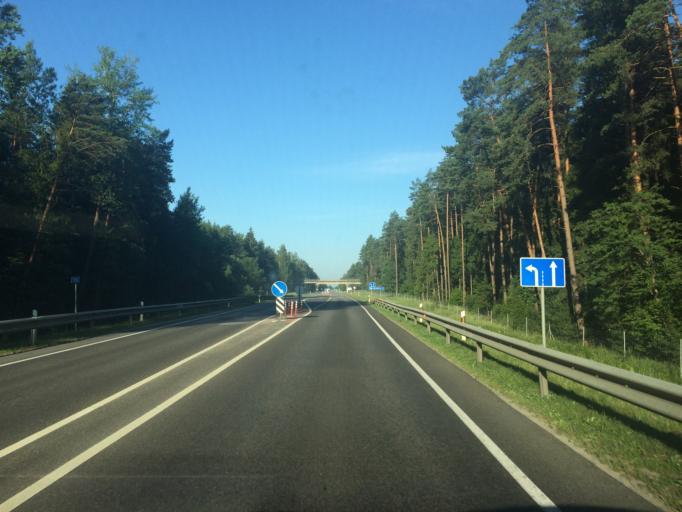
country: LT
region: Kauno apskritis
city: Jonava
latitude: 55.1590
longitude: 24.4965
